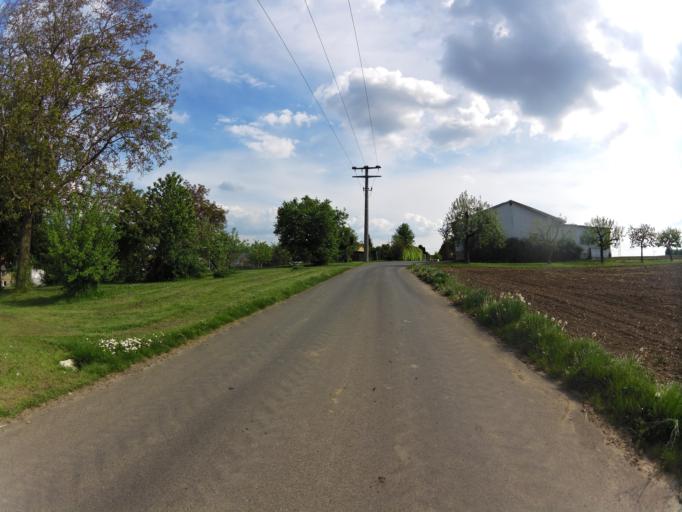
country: DE
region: Bavaria
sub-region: Regierungsbezirk Unterfranken
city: Giebelstadt
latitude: 49.6115
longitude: 9.9463
